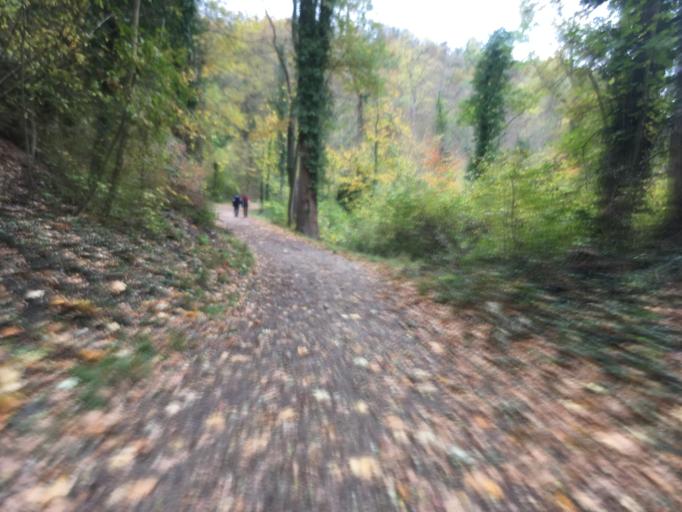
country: DE
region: Baden-Wuerttemberg
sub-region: Freiburg Region
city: Sasbach
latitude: 48.1095
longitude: 7.5881
